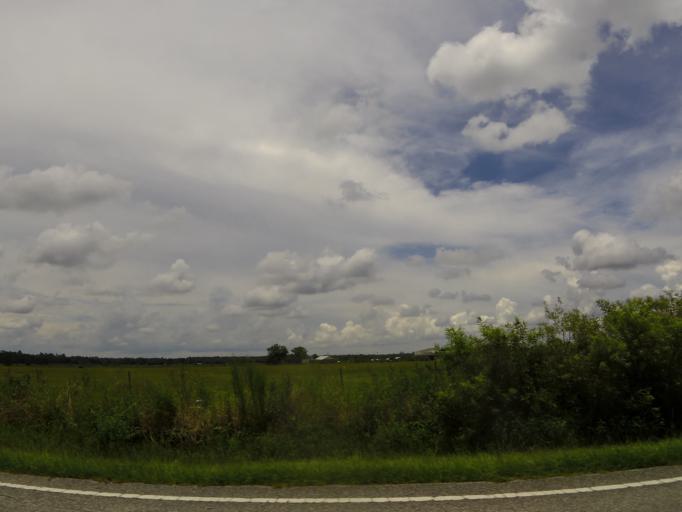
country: US
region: Florida
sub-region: Putnam County
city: East Palatka
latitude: 29.6937
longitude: -81.4866
